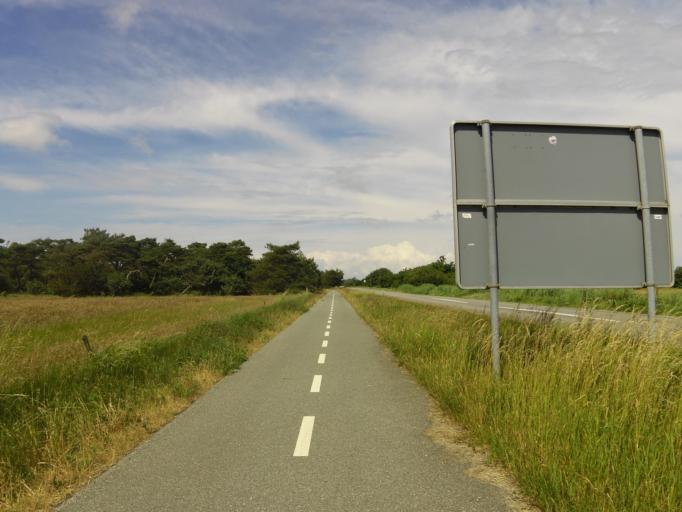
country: DE
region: Schleswig-Holstein
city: List
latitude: 55.1537
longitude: 8.5498
